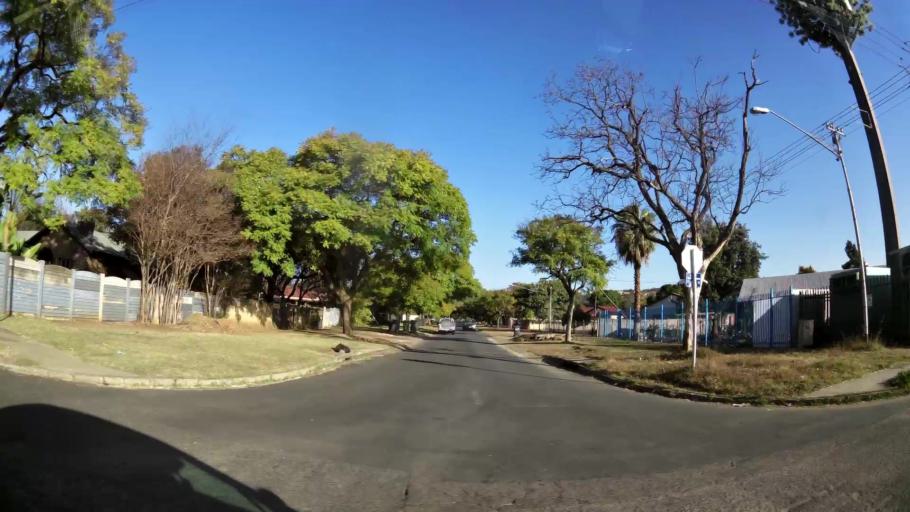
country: ZA
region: Gauteng
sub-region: City of Tshwane Metropolitan Municipality
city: Pretoria
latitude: -25.7216
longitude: 28.2124
